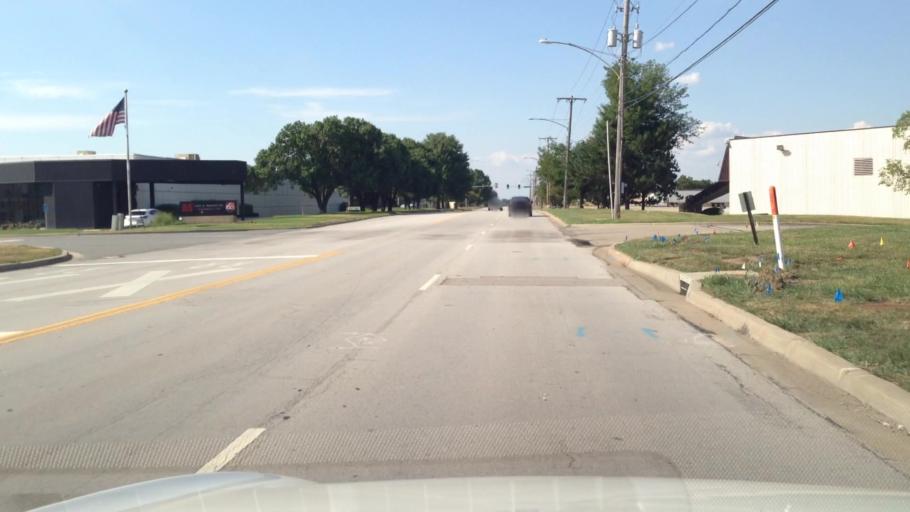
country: US
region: Kansas
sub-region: Johnson County
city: Lenexa
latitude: 38.9285
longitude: -94.7608
